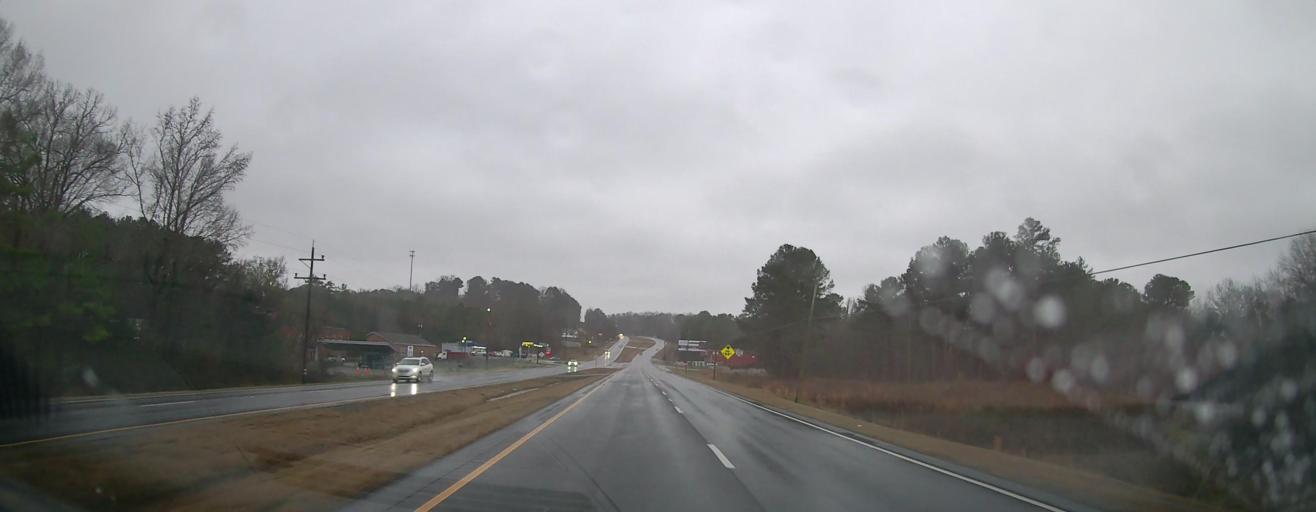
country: US
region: Alabama
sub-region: Morgan County
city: Flint City
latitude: 34.4910
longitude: -86.9651
